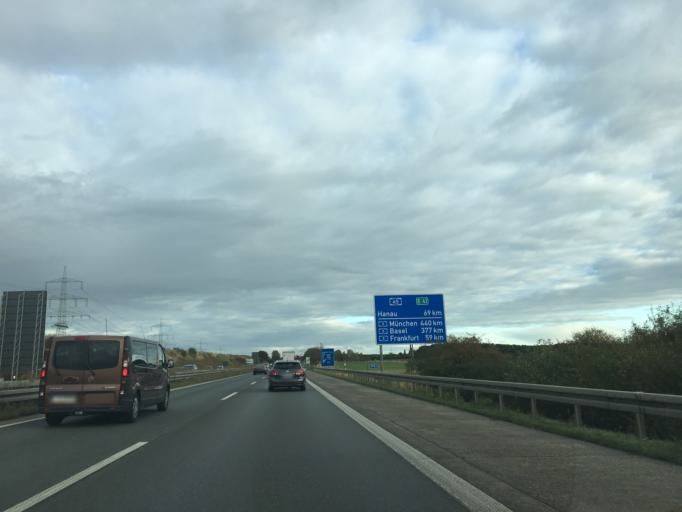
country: DE
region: Hesse
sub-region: Regierungsbezirk Giessen
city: Langgons
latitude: 50.5197
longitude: 8.6562
